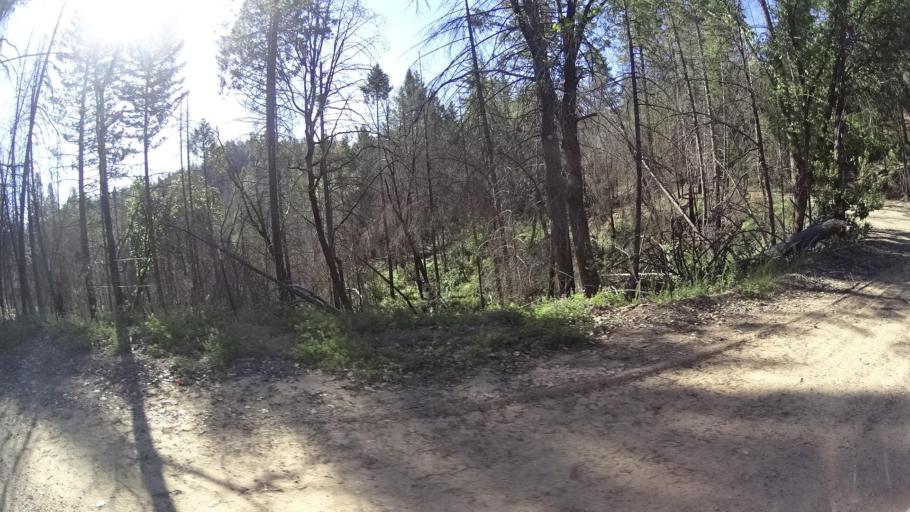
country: US
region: California
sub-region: Lake County
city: Upper Lake
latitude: 39.3807
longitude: -122.9865
